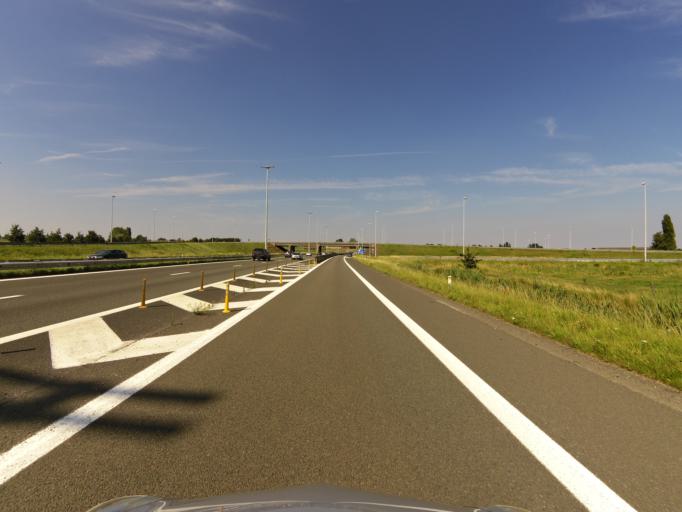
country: BE
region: Flanders
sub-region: Provincie West-Vlaanderen
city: Lichtervelde
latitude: 51.0767
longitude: 3.1534
